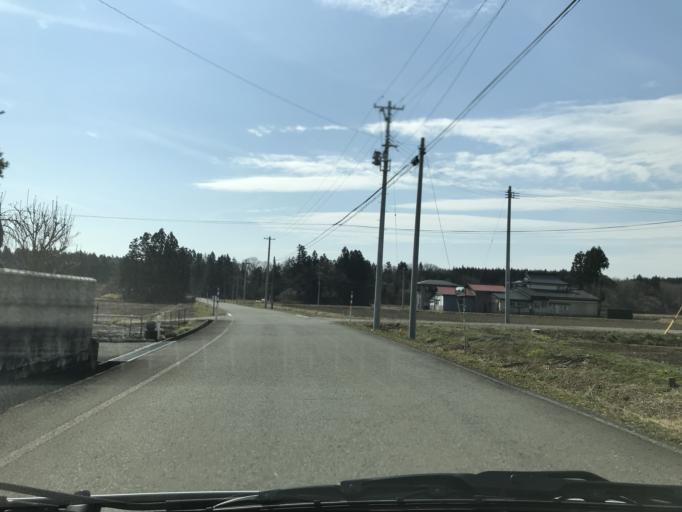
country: JP
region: Iwate
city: Mizusawa
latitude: 39.1214
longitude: 141.0431
